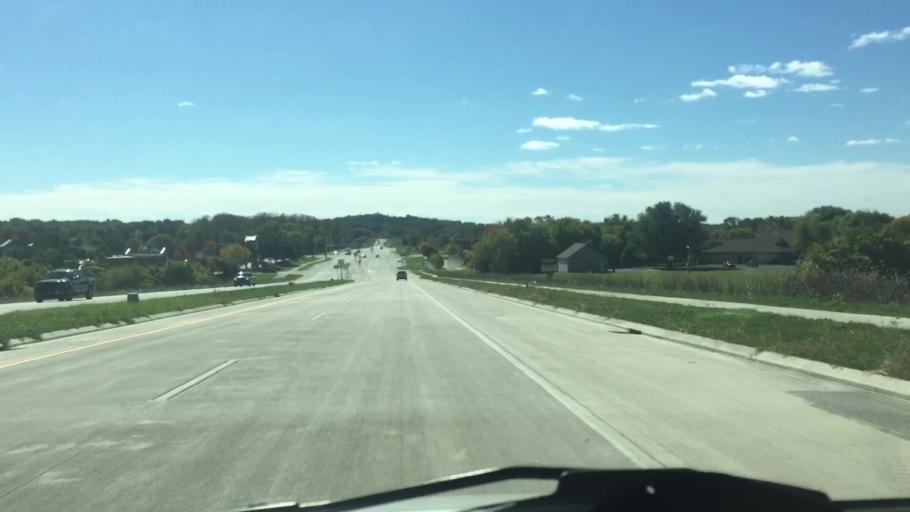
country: US
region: Wisconsin
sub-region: Waukesha County
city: Waukesha
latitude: 43.0249
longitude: -88.2860
